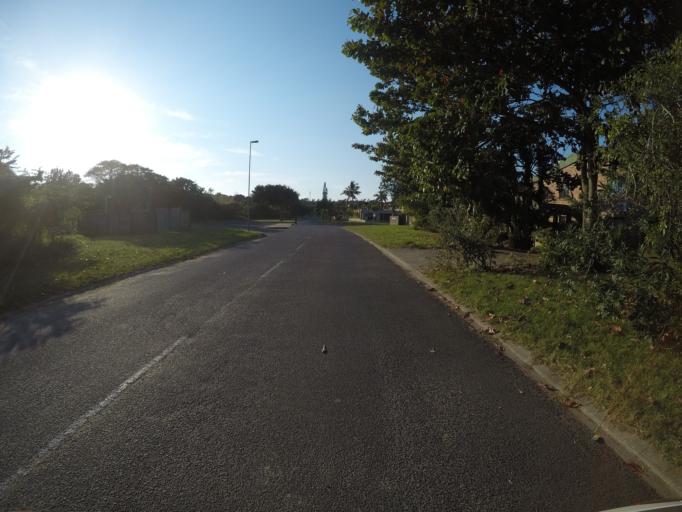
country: ZA
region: KwaZulu-Natal
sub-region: uThungulu District Municipality
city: Richards Bay
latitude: -28.7746
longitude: 32.1184
